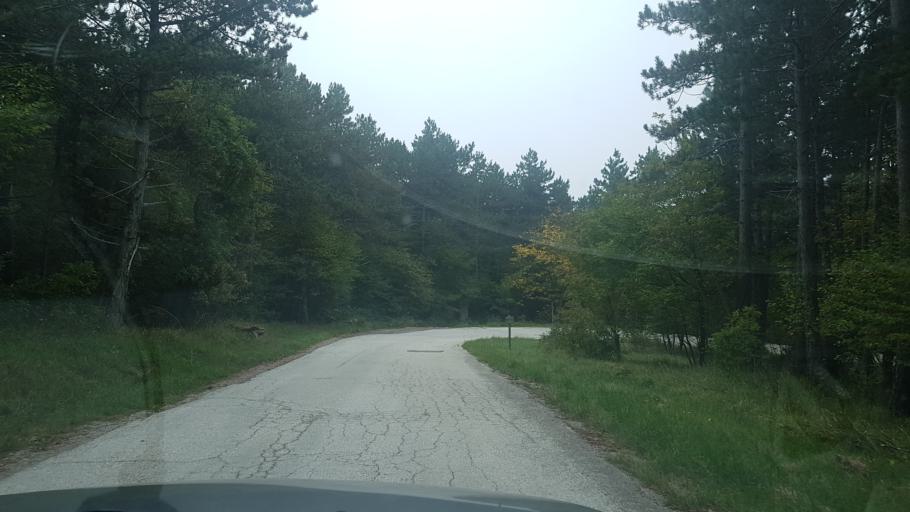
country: HR
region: Istarska
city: Buzet
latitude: 45.4513
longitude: 14.0183
